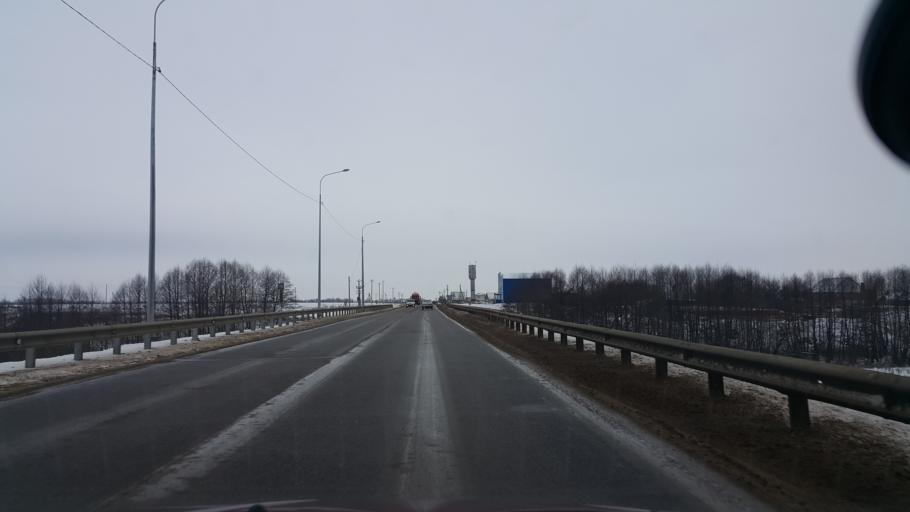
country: RU
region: Tambov
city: Bokino
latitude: 52.6163
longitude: 41.4646
